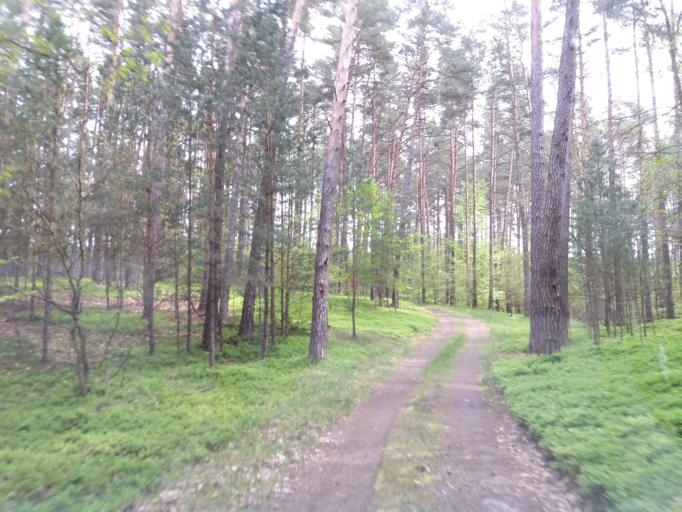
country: PL
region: West Pomeranian Voivodeship
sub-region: Powiat choszczenski
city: Bierzwnik
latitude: 52.9868
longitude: 15.6168
